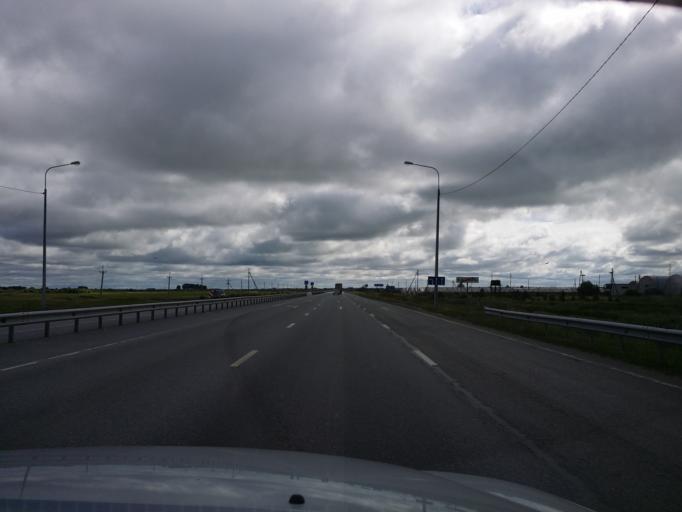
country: RU
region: Tjumen
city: Antipino
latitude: 57.1837
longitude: 65.9475
